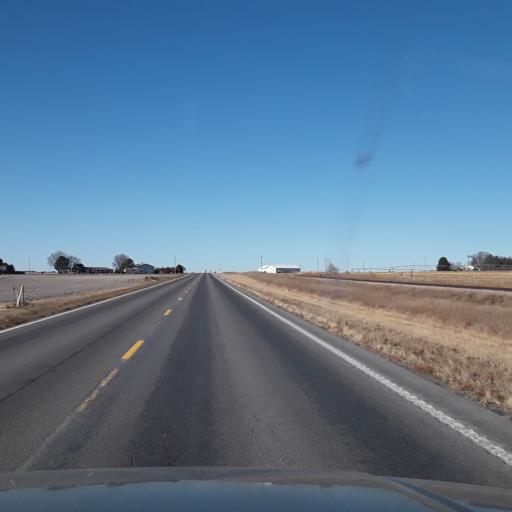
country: US
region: Nebraska
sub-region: Phelps County
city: Holdrege
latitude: 40.4485
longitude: -99.4296
